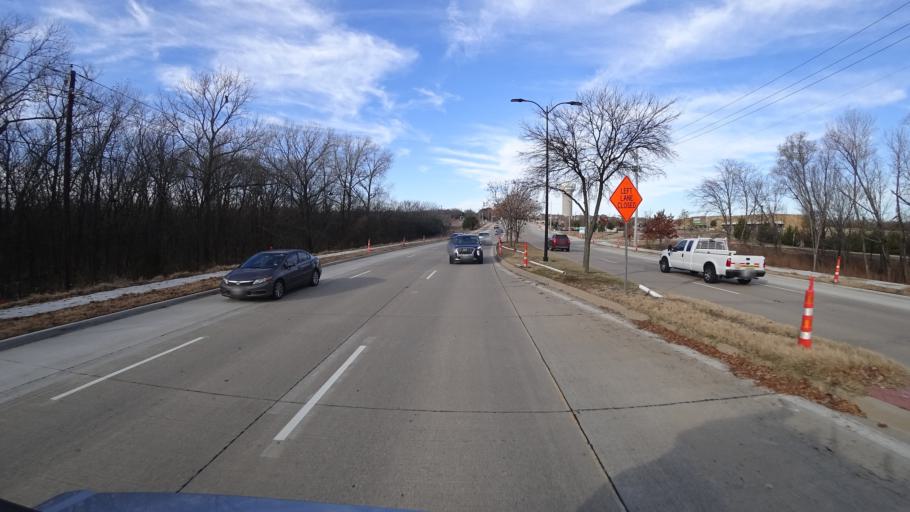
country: US
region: Texas
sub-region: Collin County
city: McKinney
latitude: 33.1964
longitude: -96.6627
